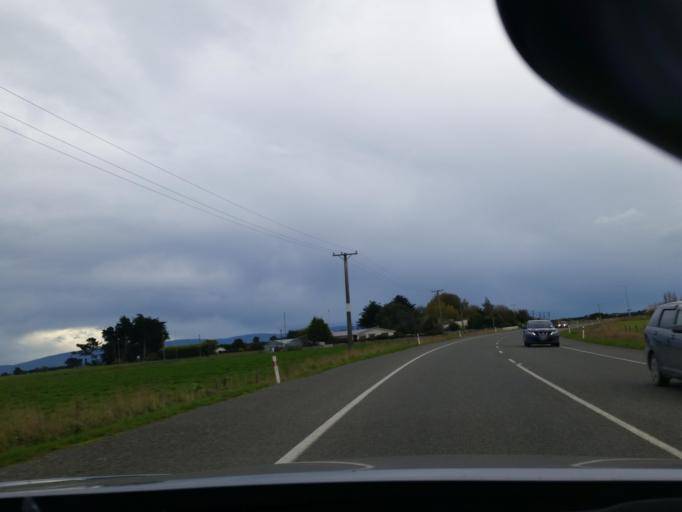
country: NZ
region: Southland
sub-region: Invercargill City
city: Invercargill
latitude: -46.3011
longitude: 168.2066
